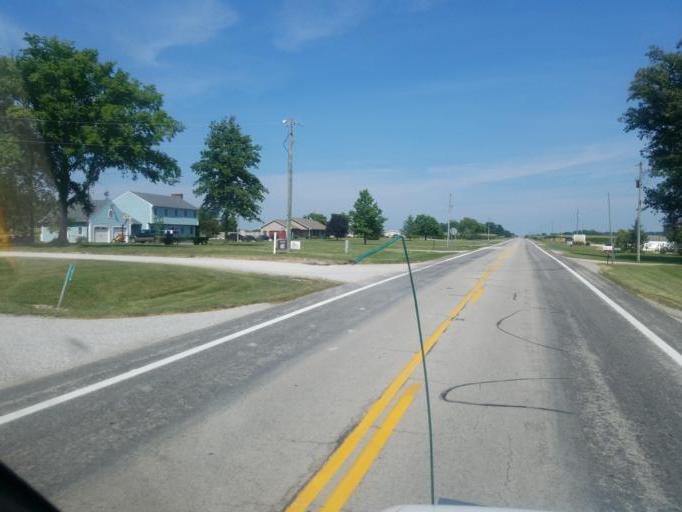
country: US
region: Ohio
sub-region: Auglaize County
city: Saint Marys
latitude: 40.4951
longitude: -84.3897
